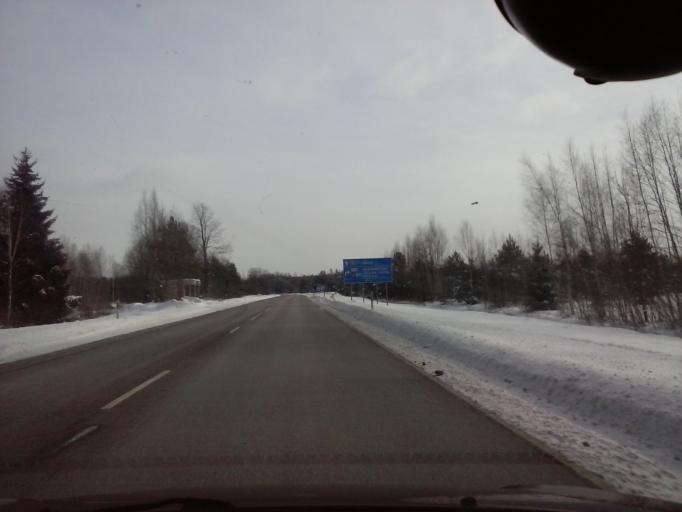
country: EE
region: Paernumaa
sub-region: Saarde vald
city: Kilingi-Nomme
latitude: 58.1718
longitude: 24.8121
